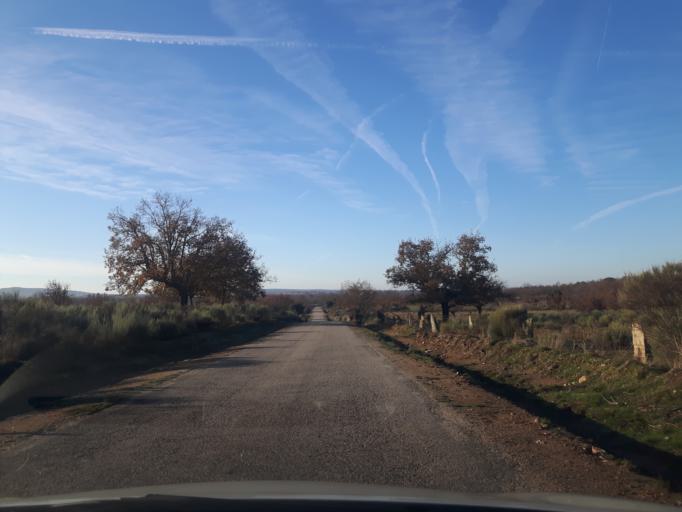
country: ES
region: Castille and Leon
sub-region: Provincia de Salamanca
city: Cerralbo
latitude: 40.9495
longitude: -6.6067
